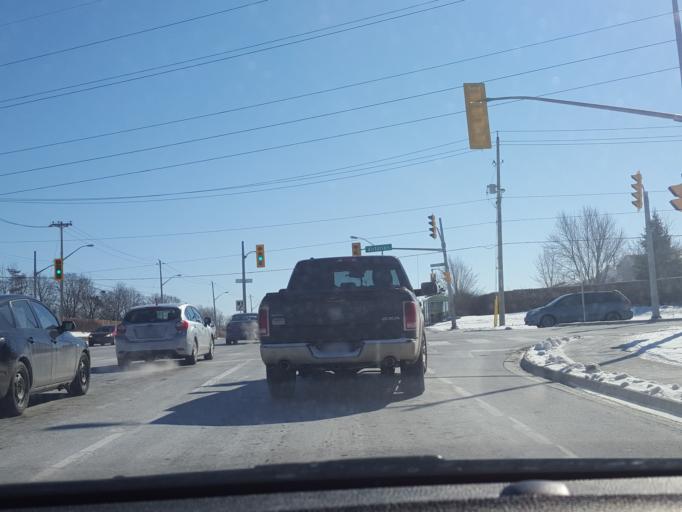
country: CA
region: Ontario
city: Kitchener
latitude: 43.4367
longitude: -80.5295
